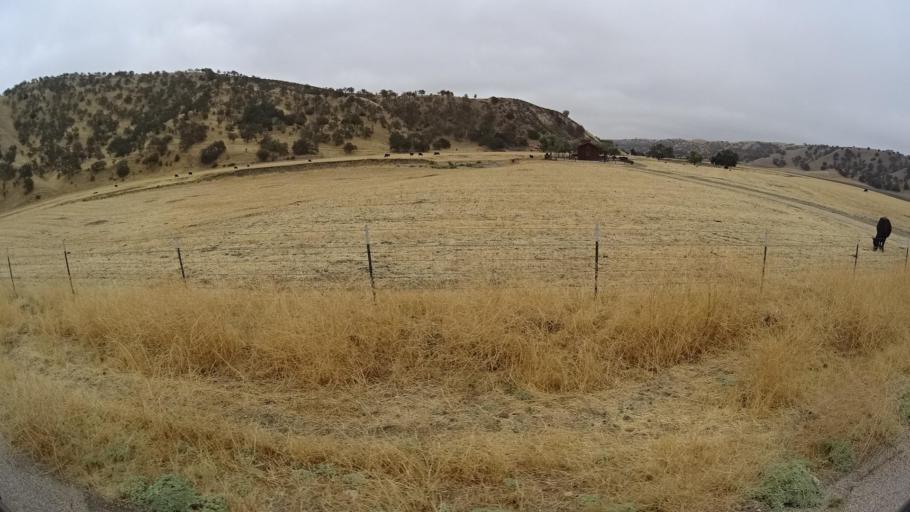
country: US
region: California
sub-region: San Luis Obispo County
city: San Miguel
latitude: 35.9076
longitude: -120.6954
